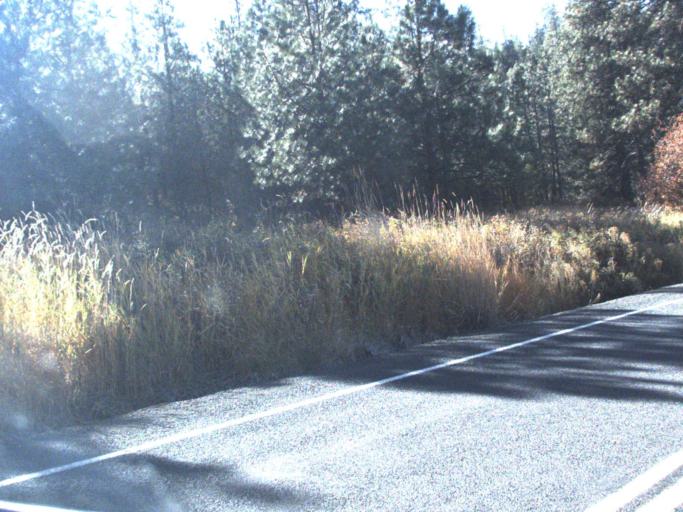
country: US
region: Washington
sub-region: Lincoln County
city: Davenport
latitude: 47.8654
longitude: -118.2604
